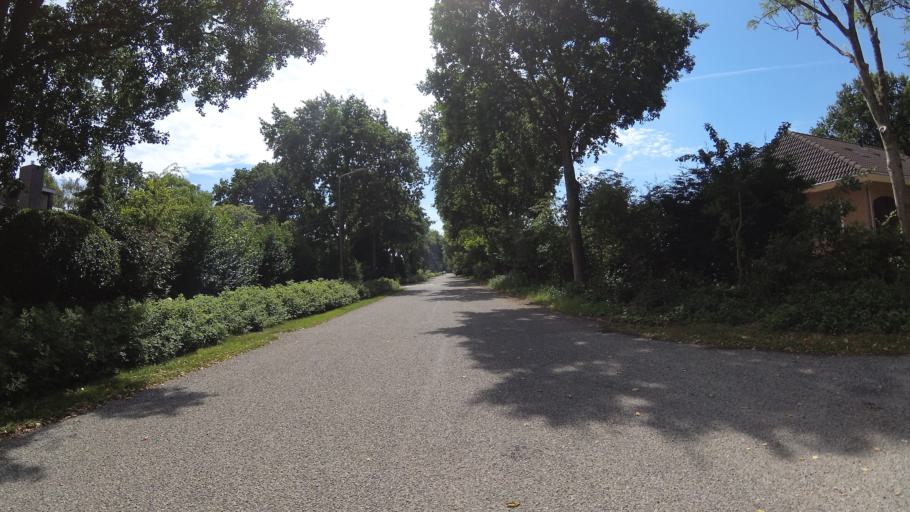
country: NL
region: Zeeland
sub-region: Gemeente Middelburg
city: Middelburg
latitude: 51.5735
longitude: 3.5456
